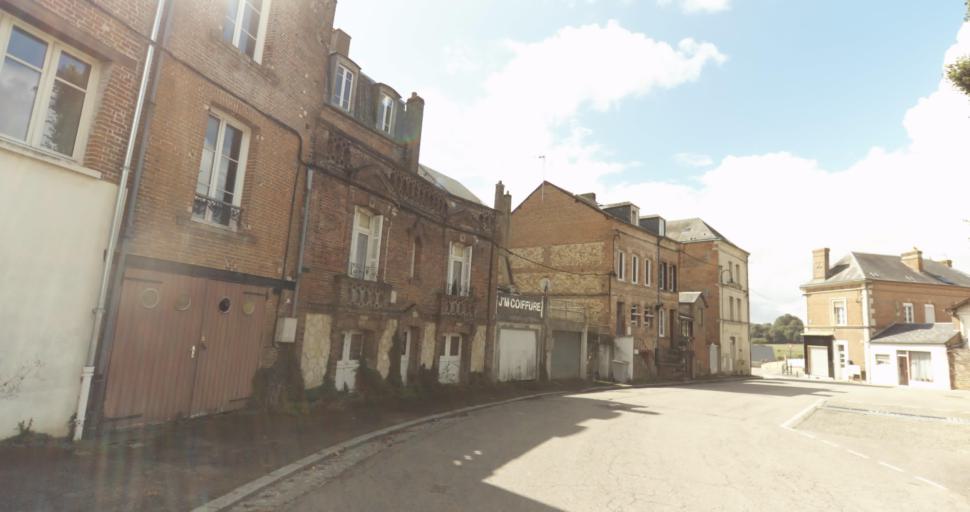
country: FR
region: Lower Normandy
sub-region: Departement de l'Orne
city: Gace
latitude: 48.7951
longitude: 0.2964
